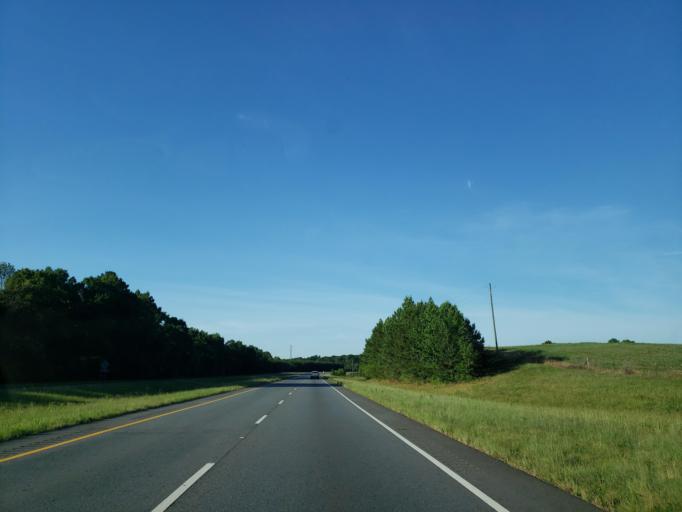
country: US
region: Georgia
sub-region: Floyd County
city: Shannon
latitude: 34.3495
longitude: -85.0734
